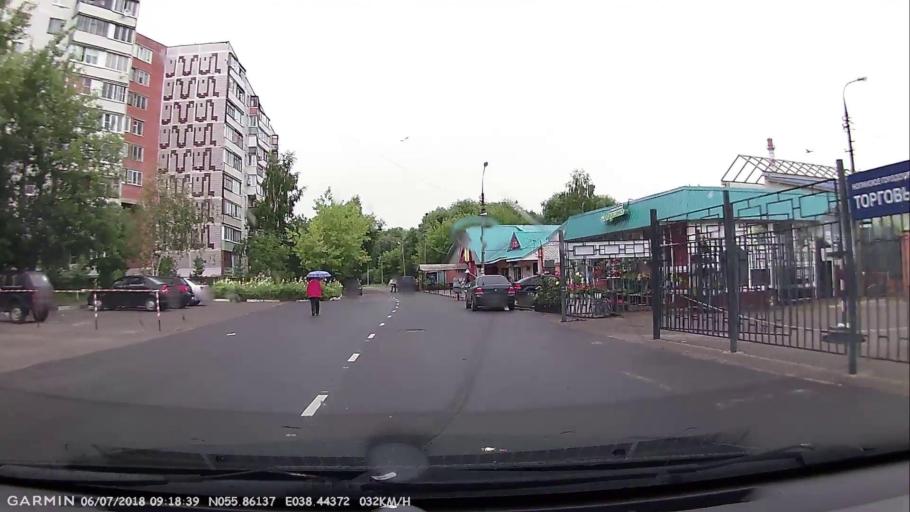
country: RU
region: Moskovskaya
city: Noginsk
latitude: 55.8614
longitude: 38.4438
